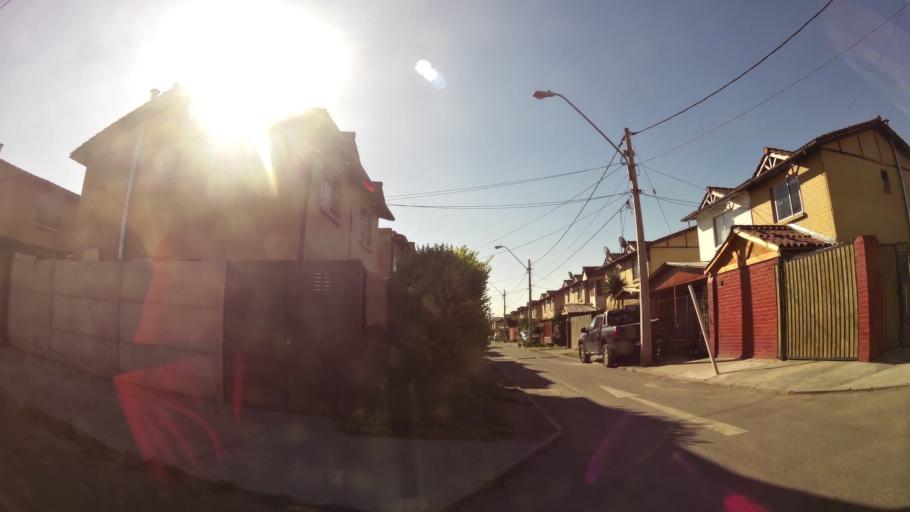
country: CL
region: Santiago Metropolitan
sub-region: Provincia de Maipo
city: San Bernardo
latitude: -33.5472
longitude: -70.7590
